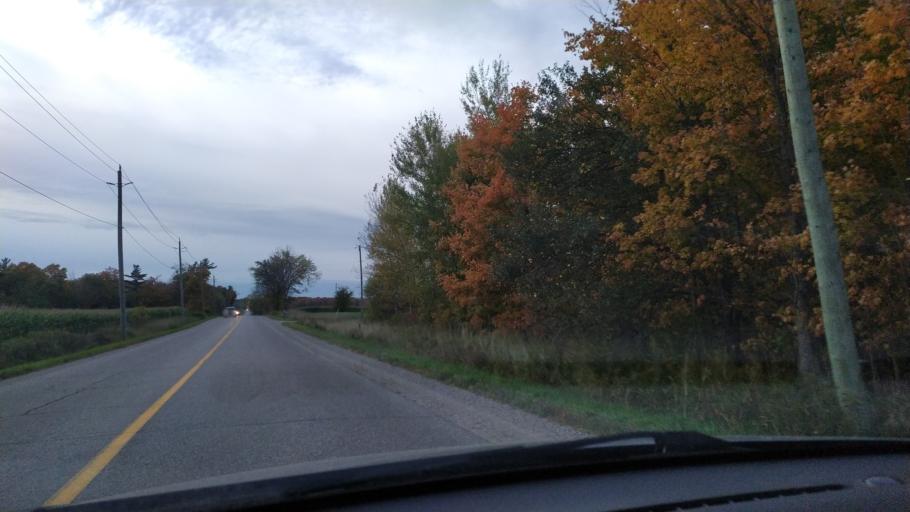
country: CA
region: Ontario
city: Waterloo
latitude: 43.5033
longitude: -80.6364
